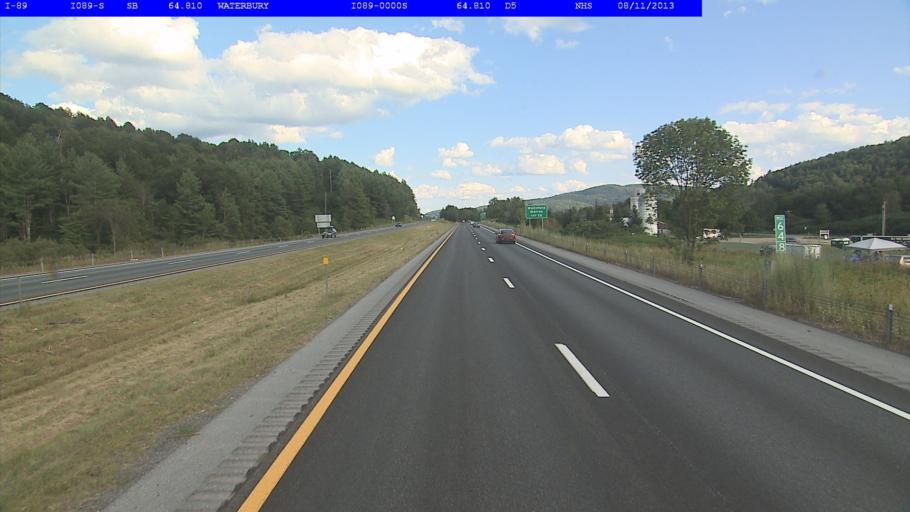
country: US
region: Vermont
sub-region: Washington County
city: Waterbury
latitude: 44.3491
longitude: -72.7708
